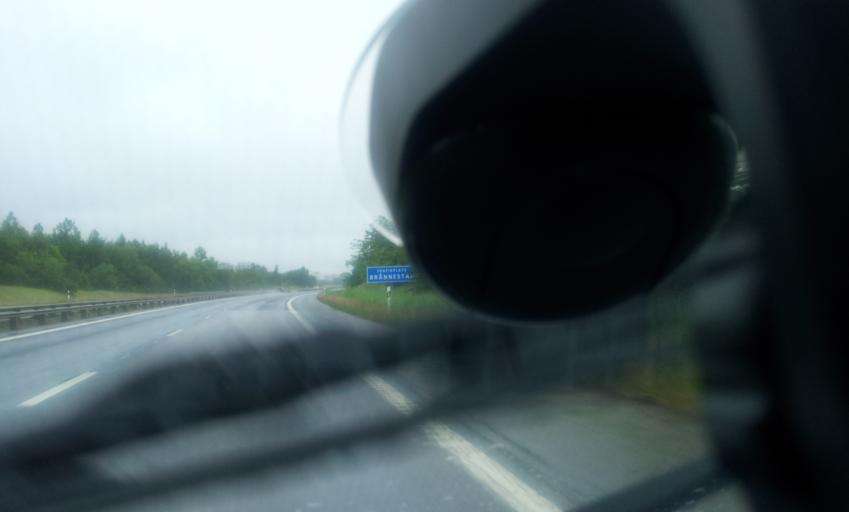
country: SE
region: OEstergoetland
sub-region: Norrkopings Kommun
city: Norrkoping
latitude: 58.5596
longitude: 16.2278
